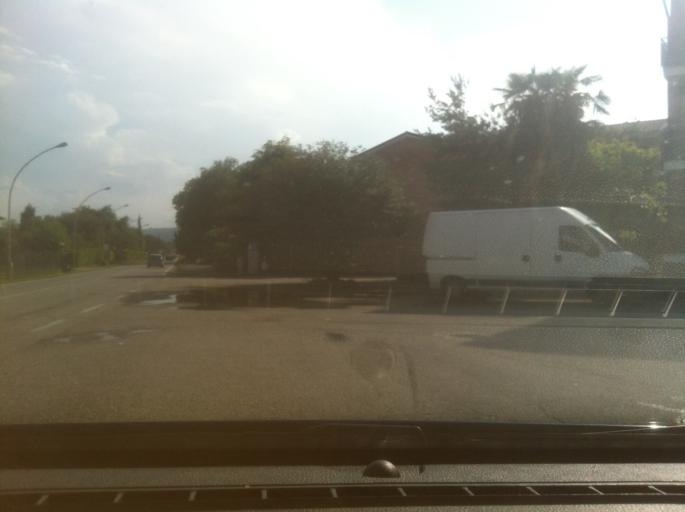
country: IT
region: Piedmont
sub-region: Provincia di Torino
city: Pavone Canavese
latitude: 45.4427
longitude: 7.8531
